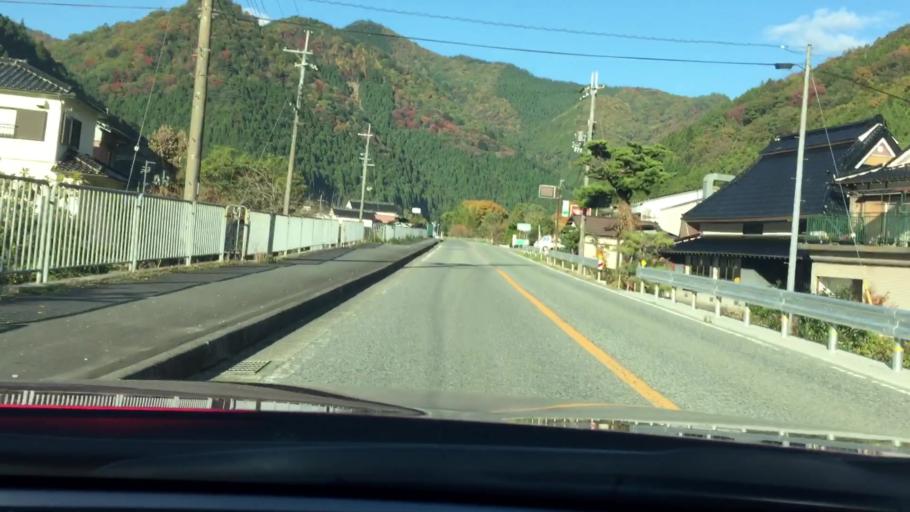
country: JP
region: Hyogo
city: Yamazakicho-nakabirose
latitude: 35.1410
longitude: 134.5502
